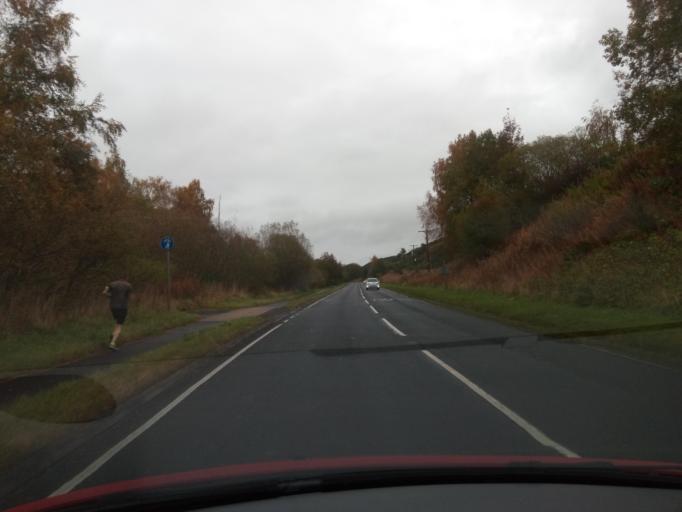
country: GB
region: Scotland
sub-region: The Scottish Borders
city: Galashiels
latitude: 55.6233
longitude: -2.8655
